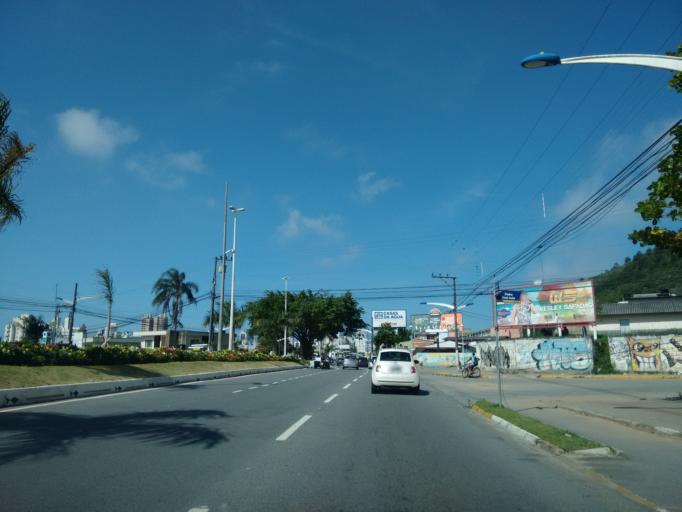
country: BR
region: Santa Catarina
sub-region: Itajai
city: Itajai
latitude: -26.9193
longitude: -48.6699
